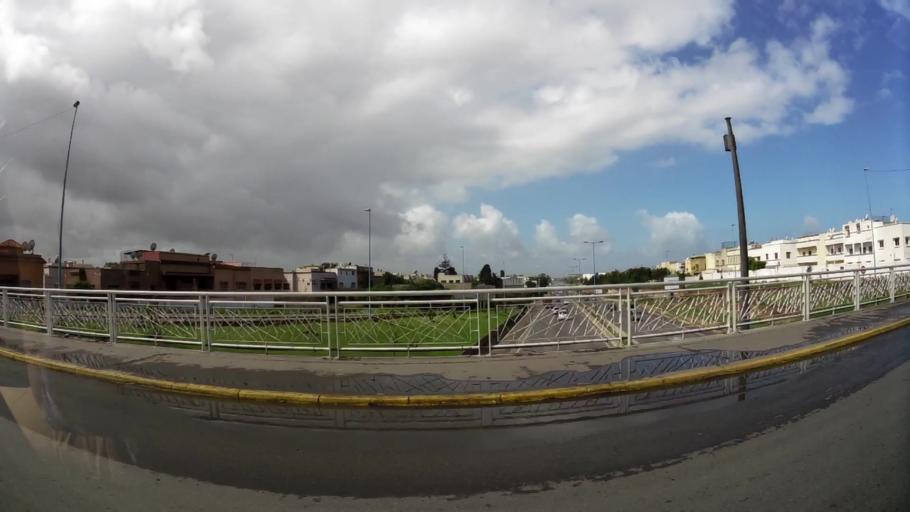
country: MA
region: Grand Casablanca
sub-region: Casablanca
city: Casablanca
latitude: 33.5569
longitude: -7.6065
